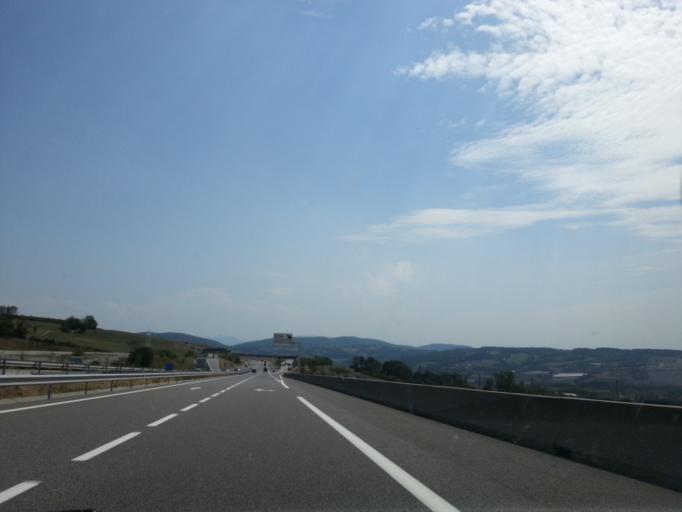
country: FR
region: Rhone-Alpes
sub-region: Departement de la Haute-Savoie
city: Cruseilles
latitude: 46.0545
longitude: 6.0798
